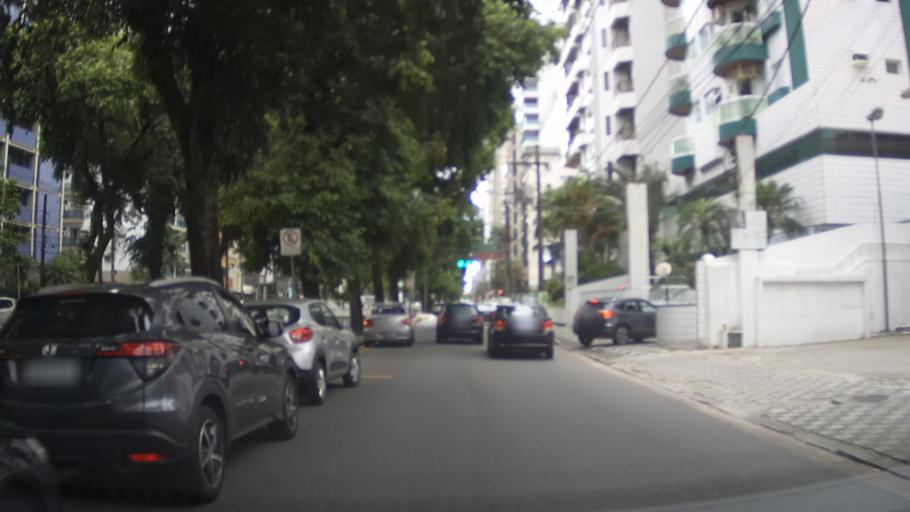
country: BR
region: Sao Paulo
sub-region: Santos
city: Santos
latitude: -23.9655
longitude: -46.3288
